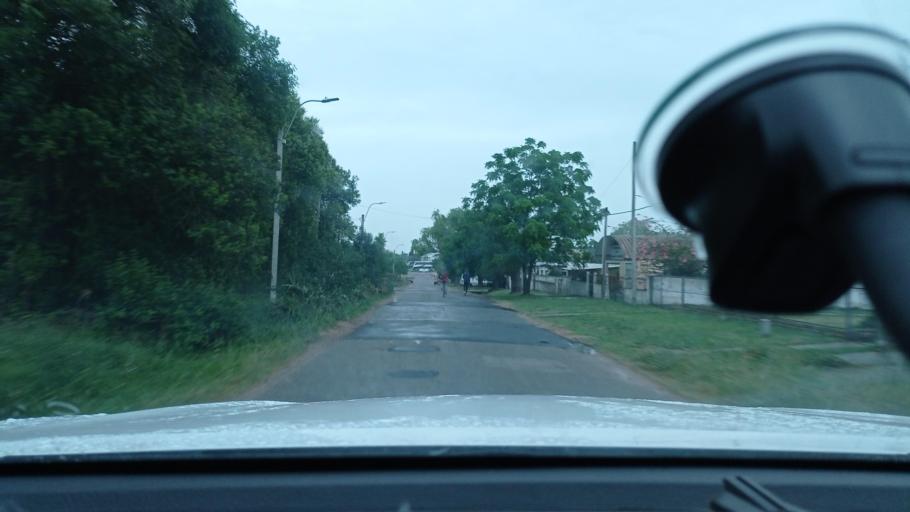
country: UY
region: Canelones
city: Joaquin Suarez
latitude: -34.7574
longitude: -56.0129
